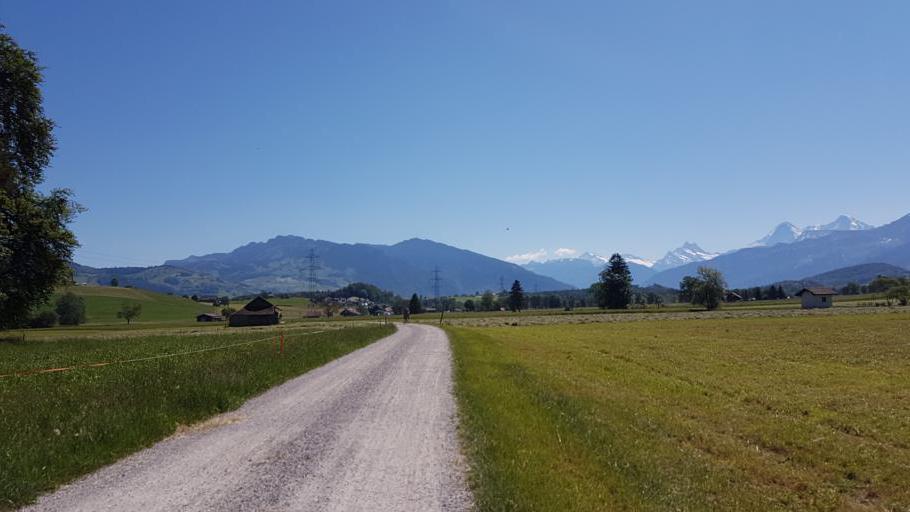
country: CH
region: Bern
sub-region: Frutigen-Niedersimmental District
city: Wimmis
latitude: 46.7037
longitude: 7.6068
